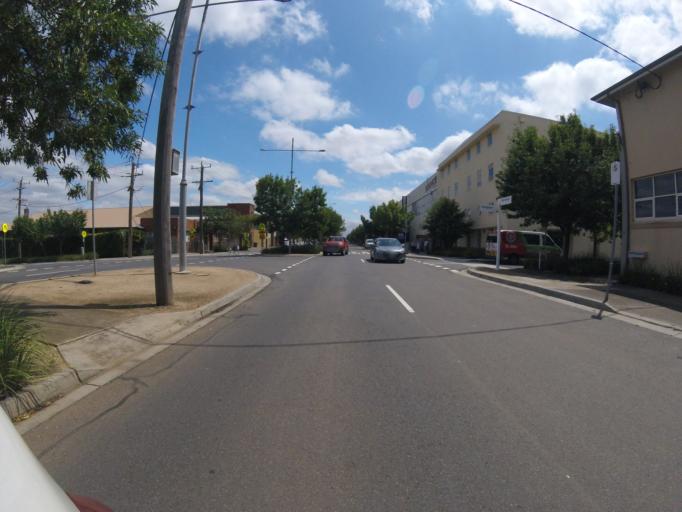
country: AU
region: Victoria
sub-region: Moonee Valley
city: Niddrie
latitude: -37.7240
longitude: 144.8978
